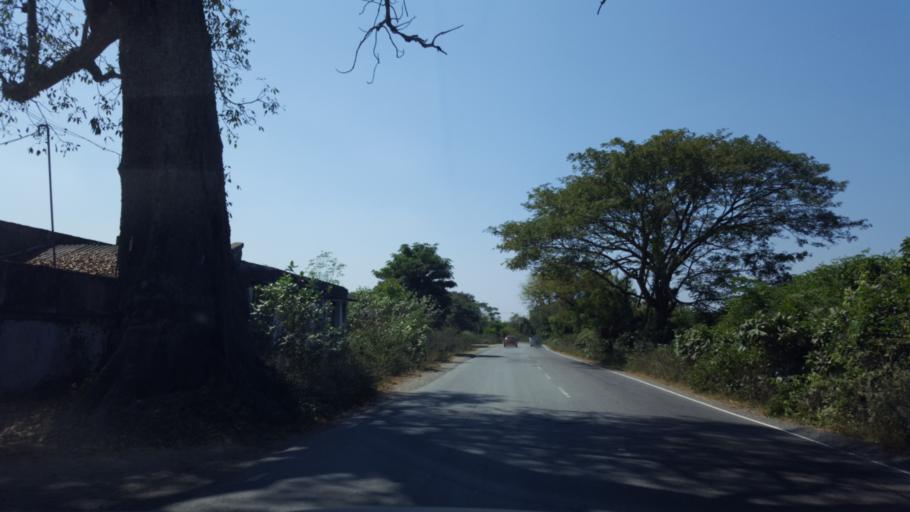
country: IN
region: Tamil Nadu
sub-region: Kancheepuram
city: Wallajahbad
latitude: 12.7813
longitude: 79.8471
